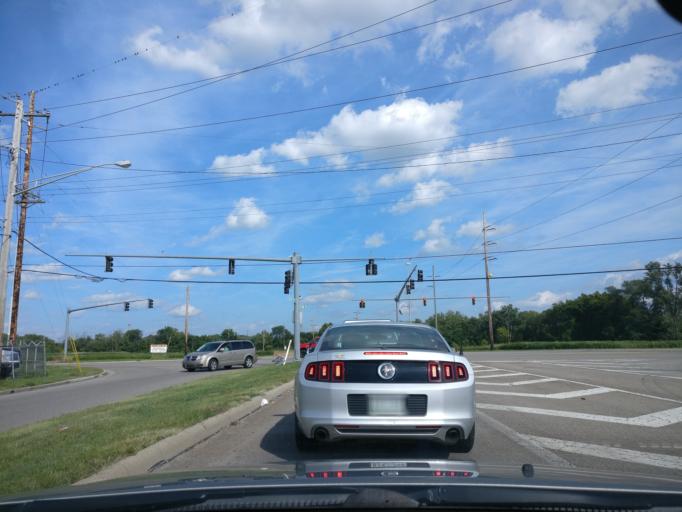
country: US
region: Ohio
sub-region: Butler County
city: Mayfield
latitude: 39.4739
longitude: -84.3436
